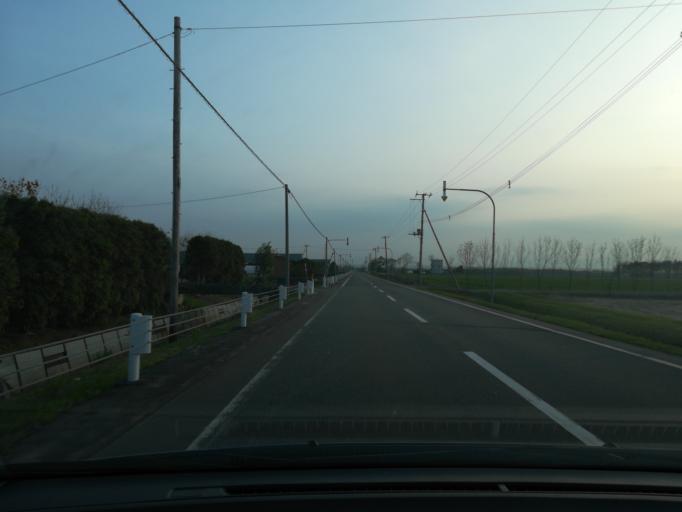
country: JP
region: Hokkaido
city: Ebetsu
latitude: 43.0777
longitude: 141.6083
